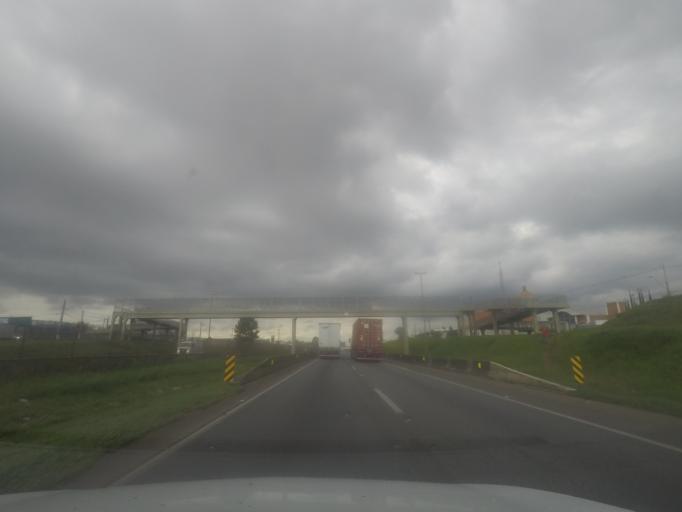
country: BR
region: Parana
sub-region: Sao Jose Dos Pinhais
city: Sao Jose dos Pinhais
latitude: -25.5474
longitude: -49.2888
